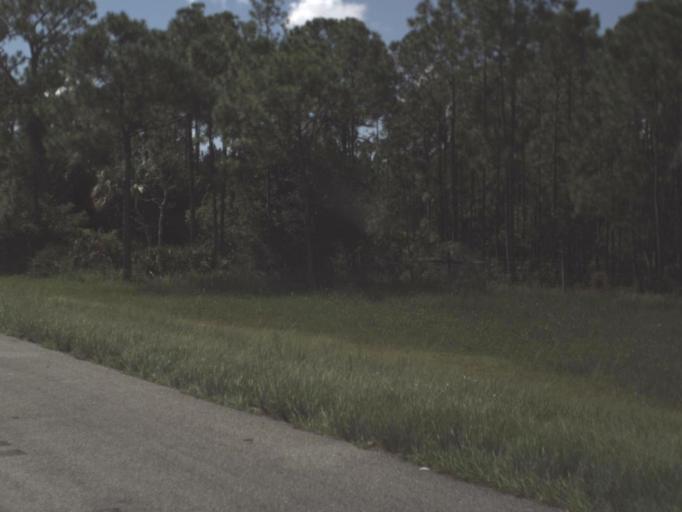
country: US
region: Florida
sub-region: Lee County
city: Suncoast Estates
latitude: 26.7860
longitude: -81.9019
